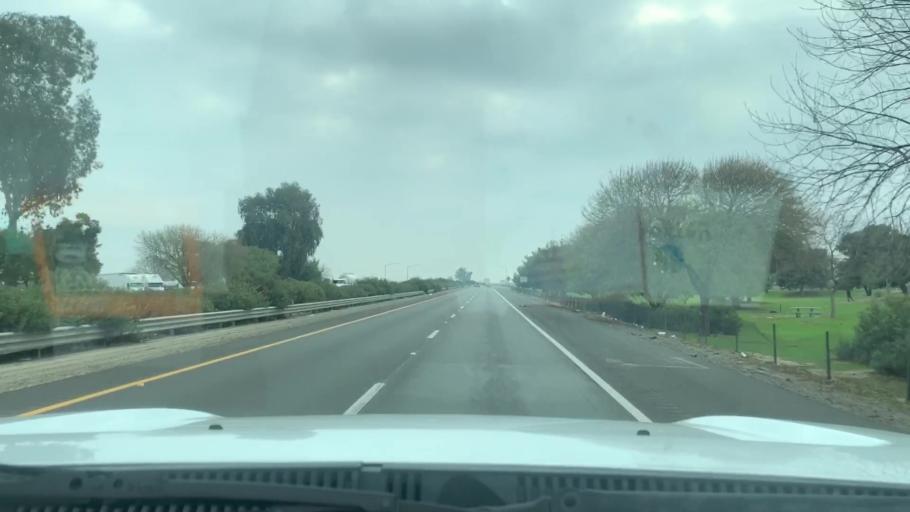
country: US
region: California
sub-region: Tulare County
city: Tipton
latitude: 36.1080
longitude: -119.3235
